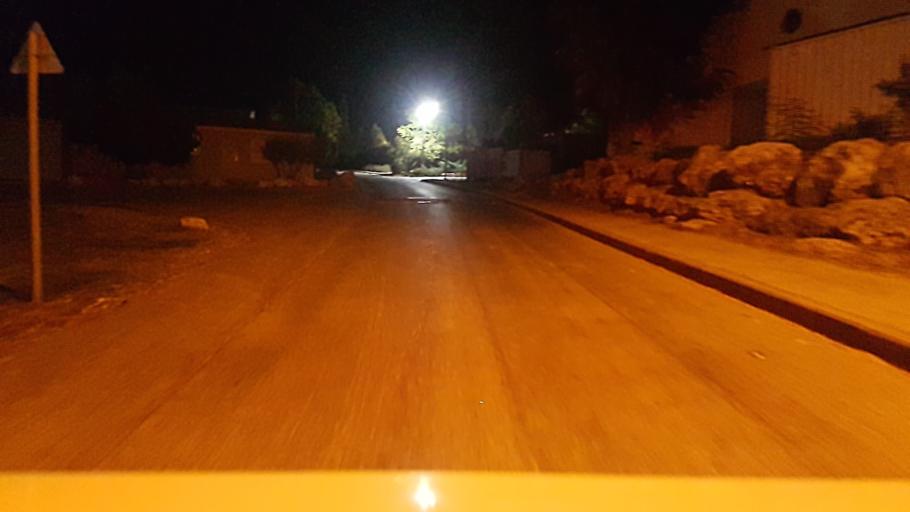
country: IL
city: Nirit
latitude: 32.1378
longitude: 34.9697
